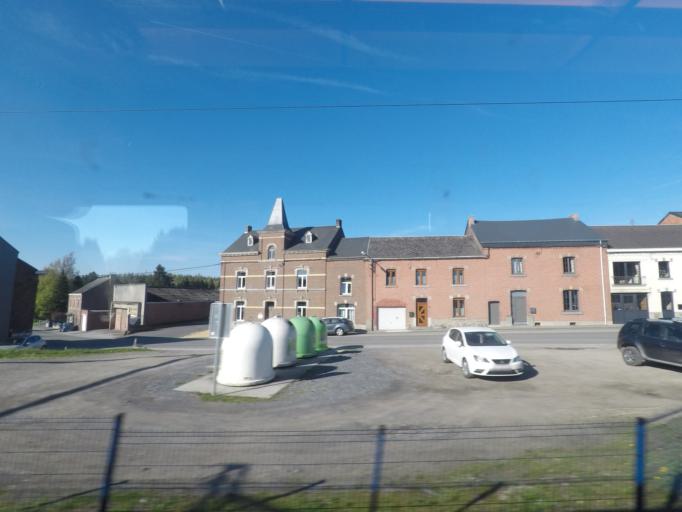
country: BE
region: Wallonia
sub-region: Province de Namur
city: Rochefort
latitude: 50.2484
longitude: 5.1950
